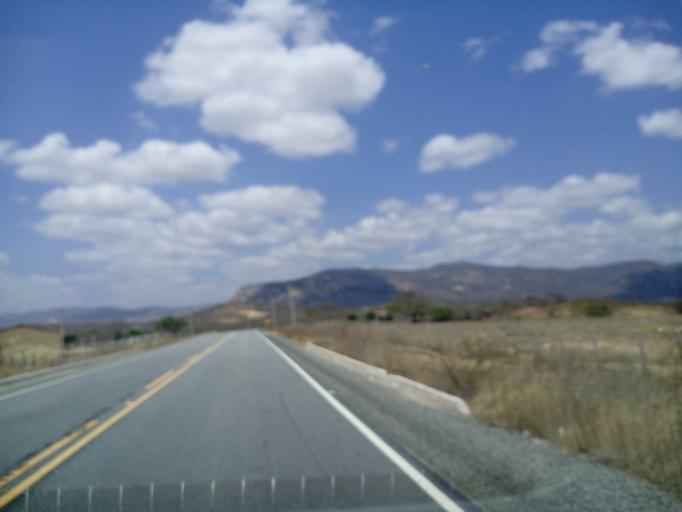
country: BR
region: Paraiba
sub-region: Desterro
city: Desterro
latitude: -7.1047
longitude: -37.0922
